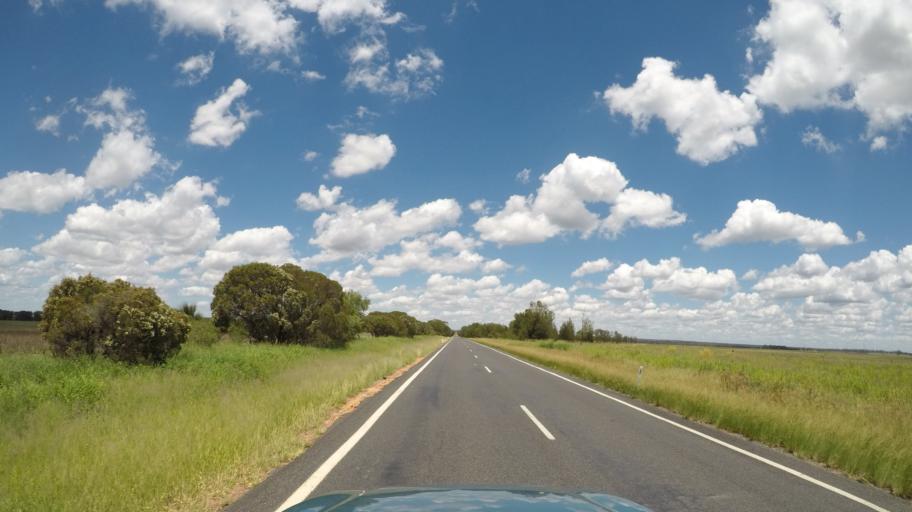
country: AU
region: Queensland
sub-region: Goondiwindi
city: Goondiwindi
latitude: -28.0042
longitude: 150.8912
